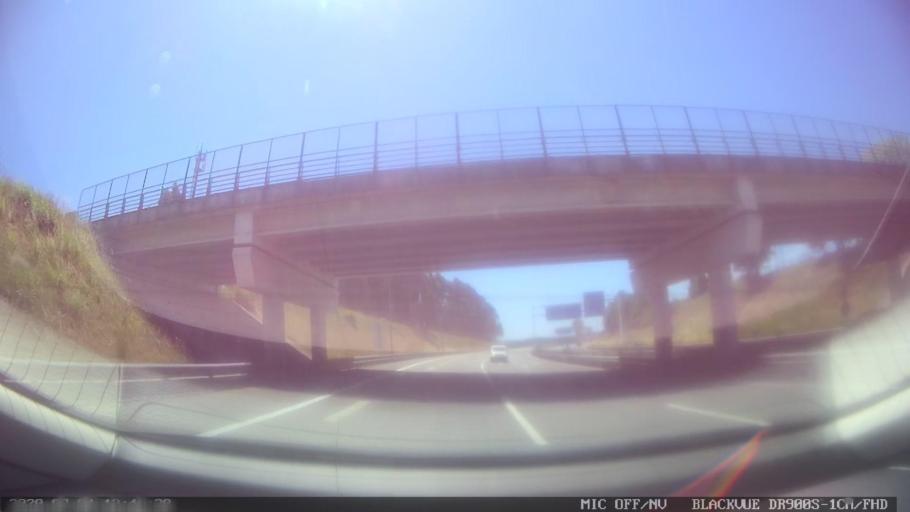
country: PT
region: Porto
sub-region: Matosinhos
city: Santa Cruz do Bispo
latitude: 41.2268
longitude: -8.6580
